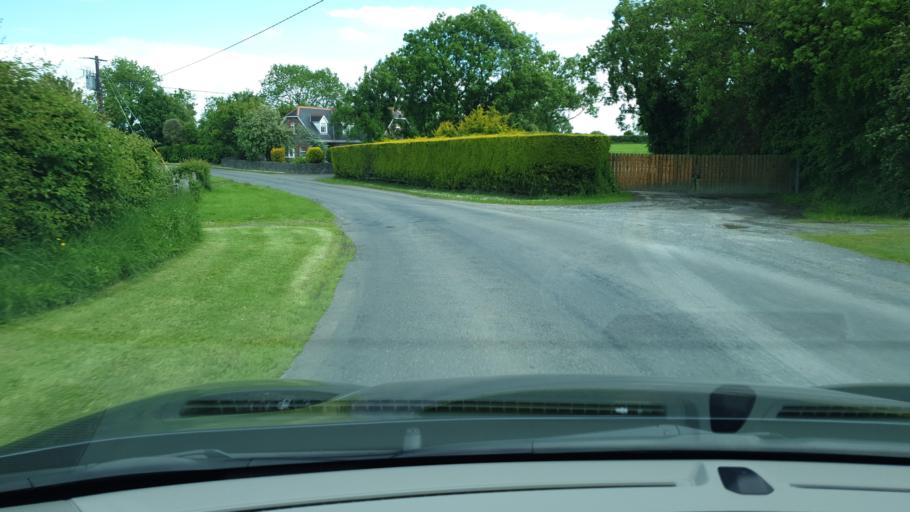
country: IE
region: Leinster
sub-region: An Mhi
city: Navan
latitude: 53.7915
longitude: -6.6841
